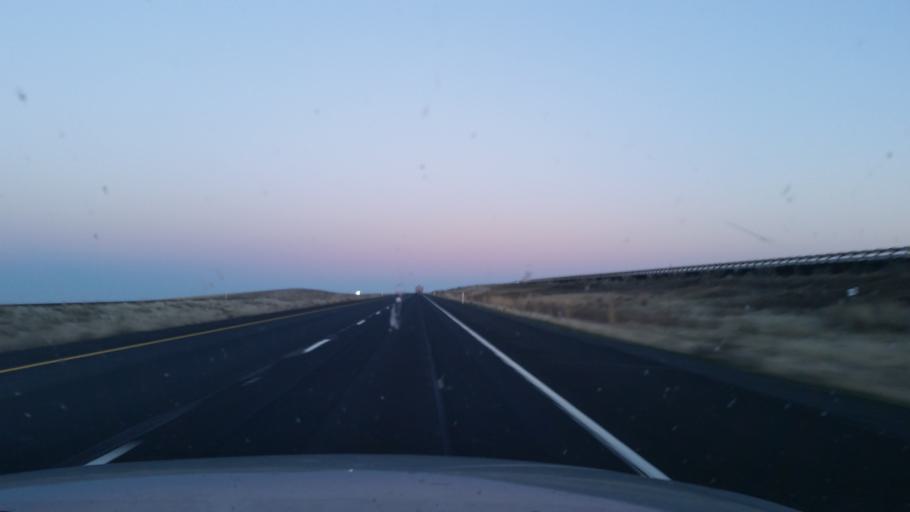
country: US
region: Washington
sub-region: Adams County
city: Ritzville
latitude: 47.1103
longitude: -118.5466
